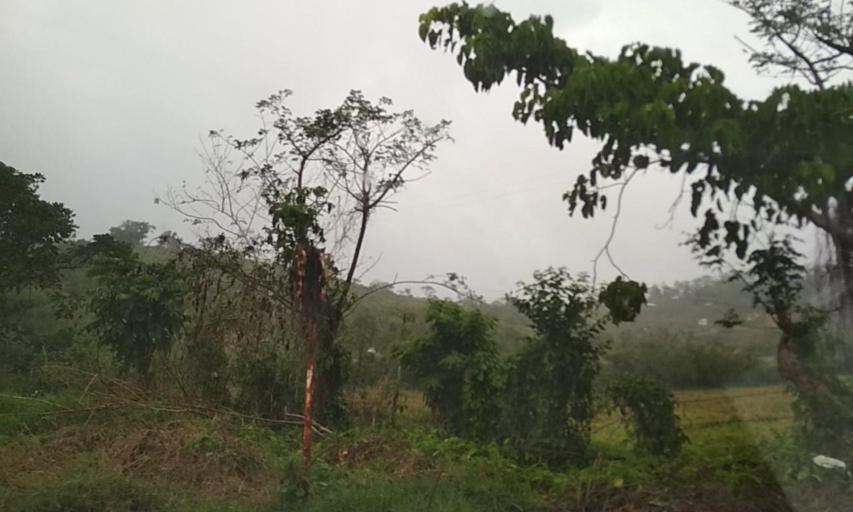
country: MX
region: Veracruz
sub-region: Papantla
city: El Chote
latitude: 20.3930
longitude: -97.3262
